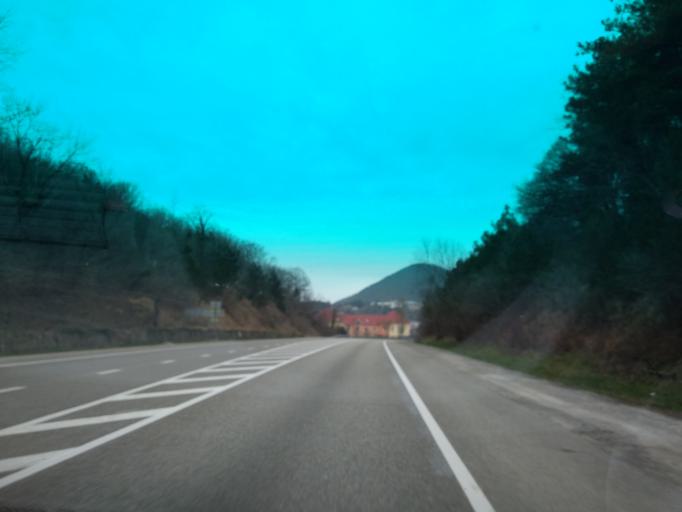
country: RU
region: Krasnodarskiy
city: Ol'ginka
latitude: 44.1894
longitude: 38.8899
